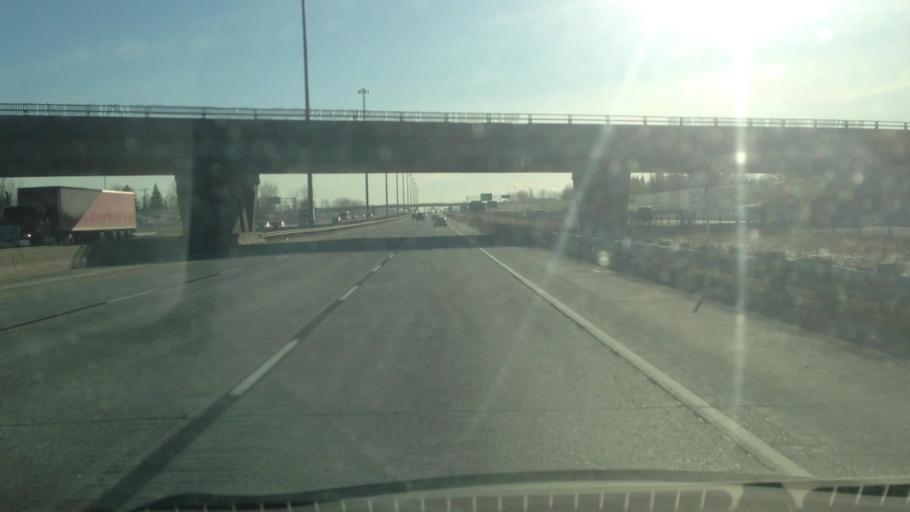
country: CA
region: Quebec
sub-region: Laurentides
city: Boisbriand
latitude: 45.5740
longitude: -73.8305
